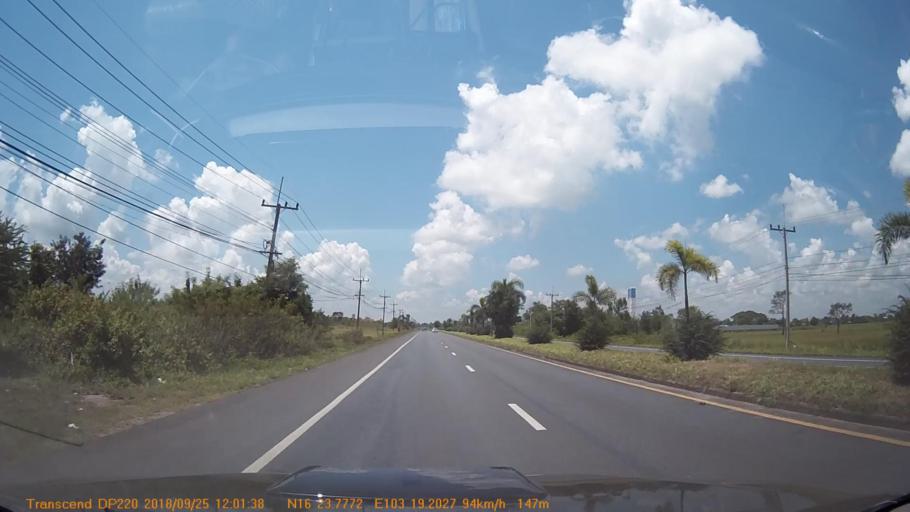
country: TH
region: Kalasin
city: Yang Talat
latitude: 16.3963
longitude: 103.3199
